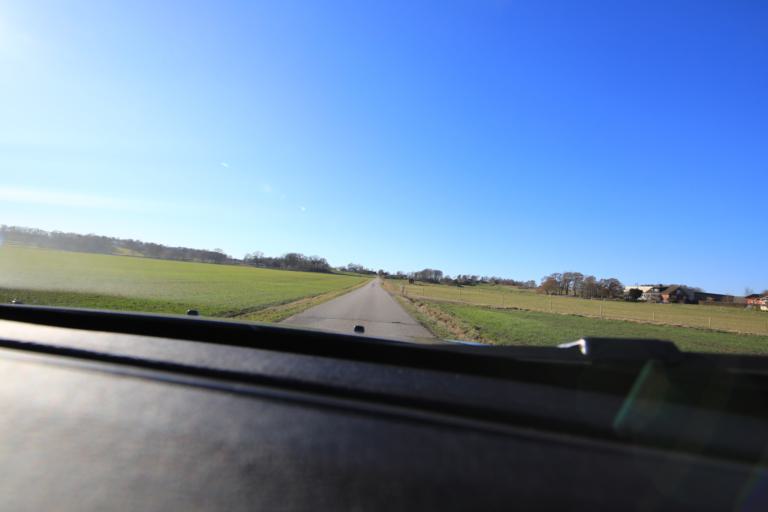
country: SE
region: Halland
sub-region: Varbergs Kommun
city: Tvaaker
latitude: 57.0644
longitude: 12.4018
